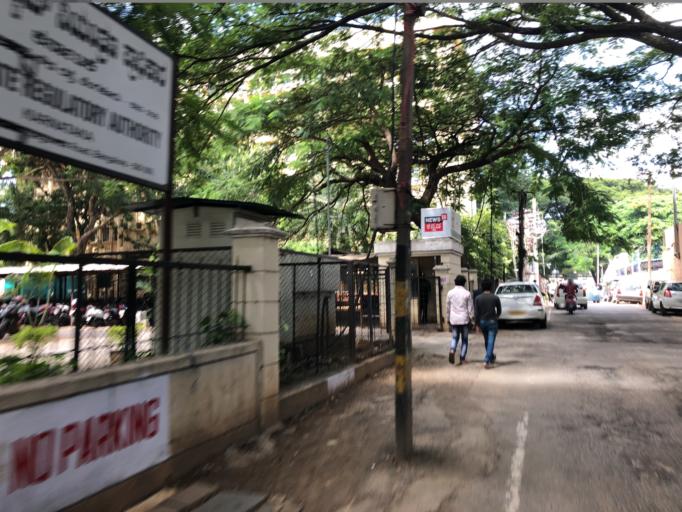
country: IN
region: Karnataka
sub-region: Bangalore Urban
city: Bangalore
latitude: 12.9632
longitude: 77.5879
